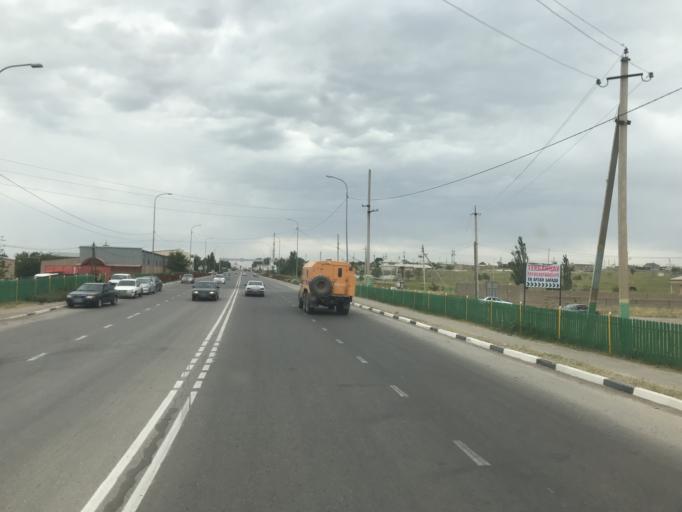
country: KZ
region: Ongtustik Qazaqstan
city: Saryaghash
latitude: 41.4732
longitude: 69.1810
